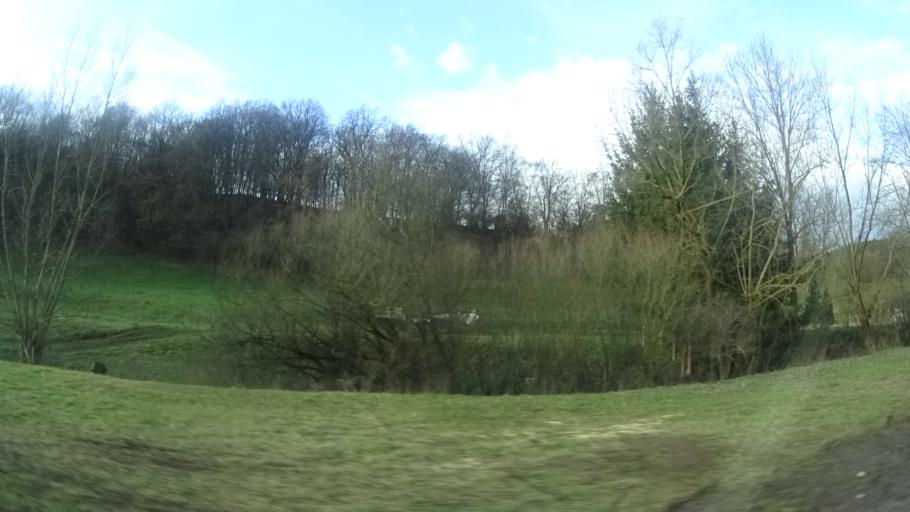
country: DE
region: Thuringia
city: Rottenbach
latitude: 50.7143
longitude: 11.1983
